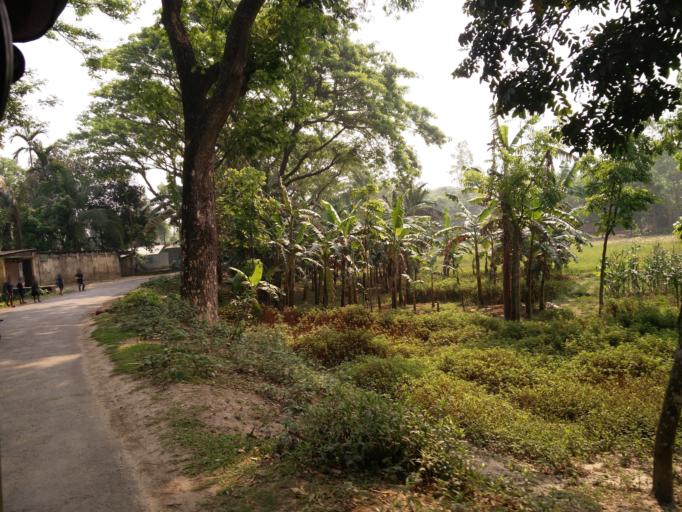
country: BD
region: Dhaka
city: Muktagacha
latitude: 24.9083
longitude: 90.2069
